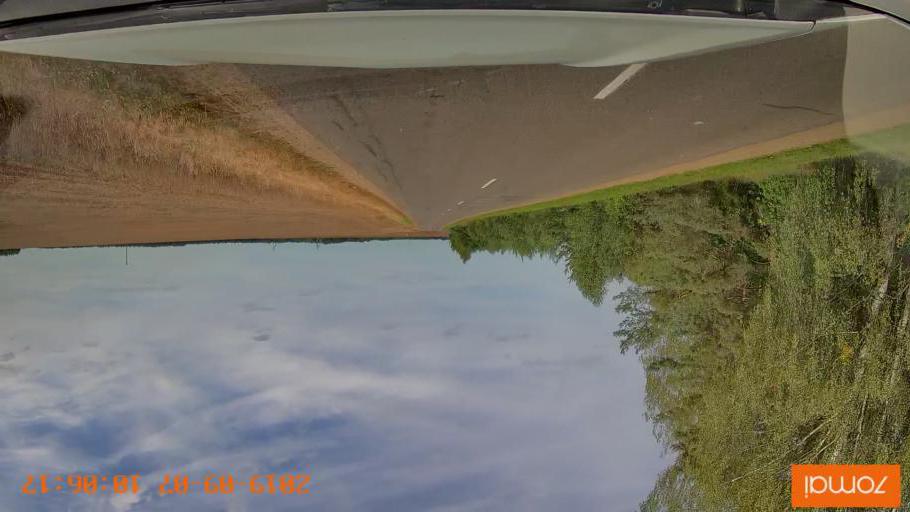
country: BY
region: Grodnenskaya
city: Voranava
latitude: 54.0596
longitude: 25.4032
